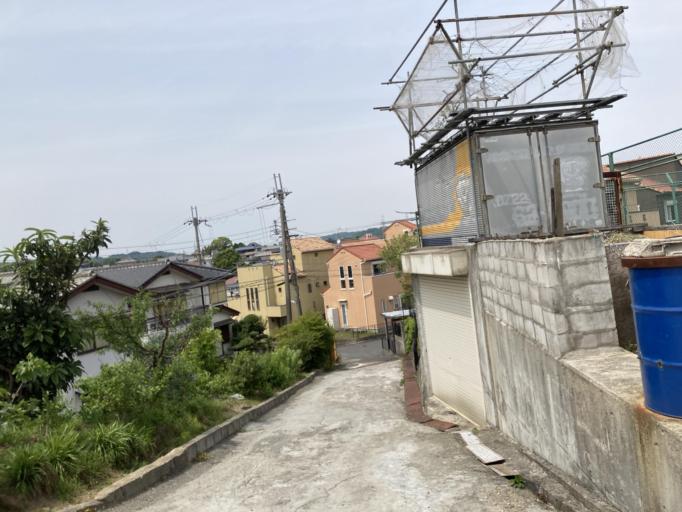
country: JP
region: Nara
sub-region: Ikoma-shi
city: Ikoma
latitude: 34.7145
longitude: 135.7005
